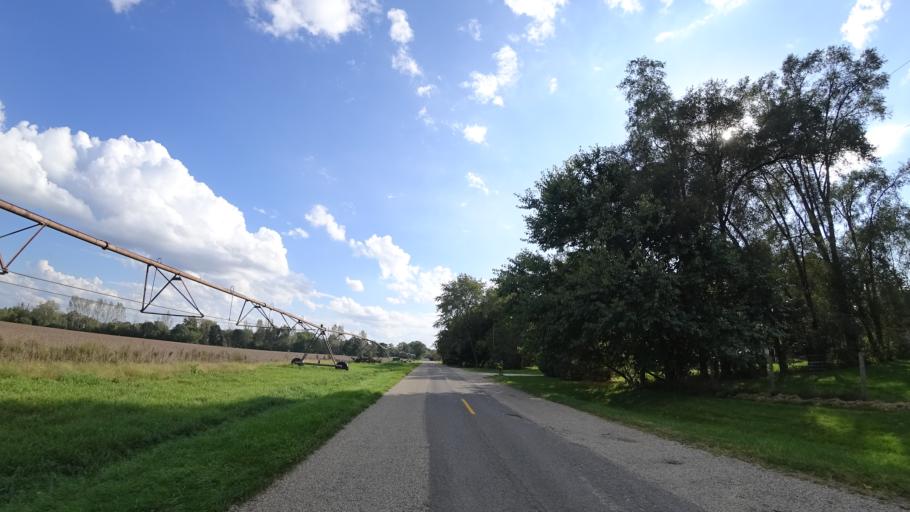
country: US
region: Michigan
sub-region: Saint Joseph County
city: Three Rivers
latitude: 41.9458
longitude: -85.6042
